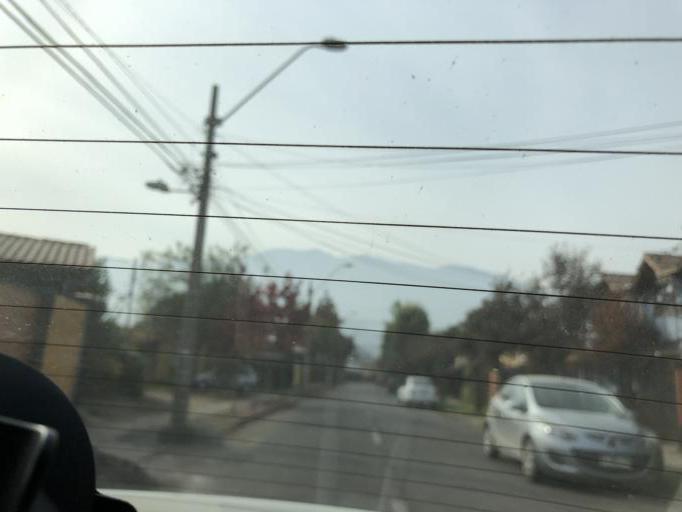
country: CL
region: Santiago Metropolitan
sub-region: Provincia de Cordillera
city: Puente Alto
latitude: -33.5519
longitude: -70.5591
